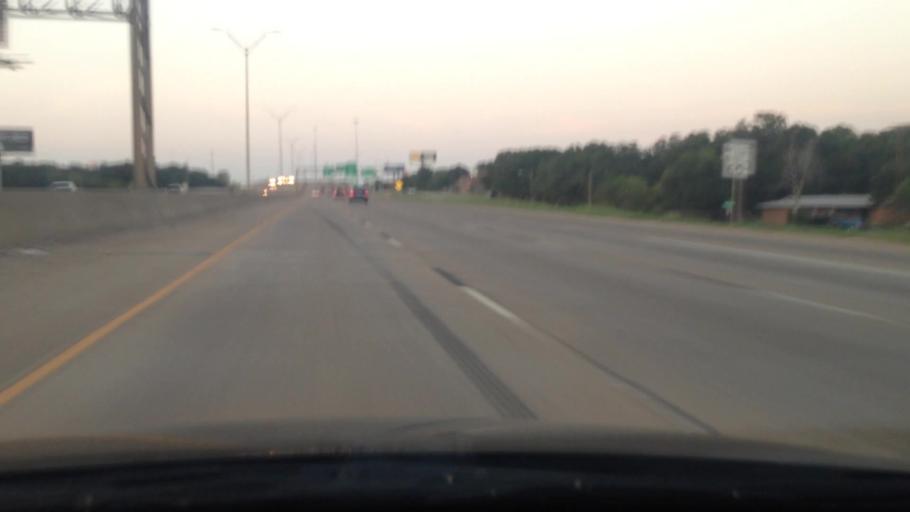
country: US
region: Texas
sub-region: Tarrant County
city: Richland Hills
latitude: 32.7487
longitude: -97.2204
